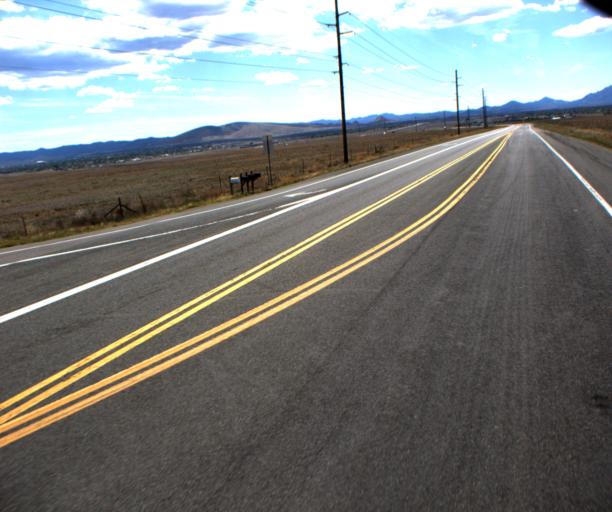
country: US
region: Arizona
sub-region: Yavapai County
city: Prescott Valley
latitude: 34.6527
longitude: -112.2837
